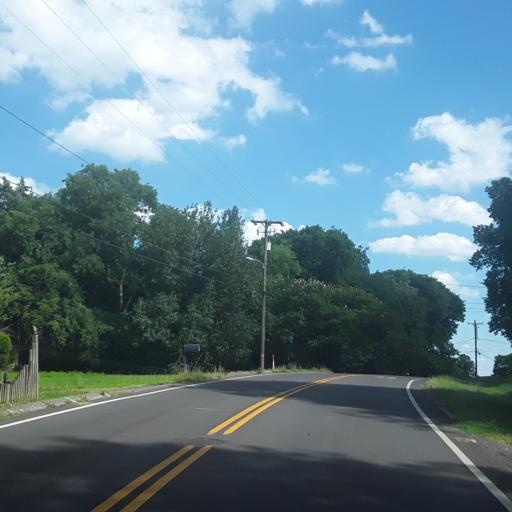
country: US
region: Tennessee
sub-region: Davidson County
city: Lakewood
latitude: 36.1921
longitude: -86.6310
